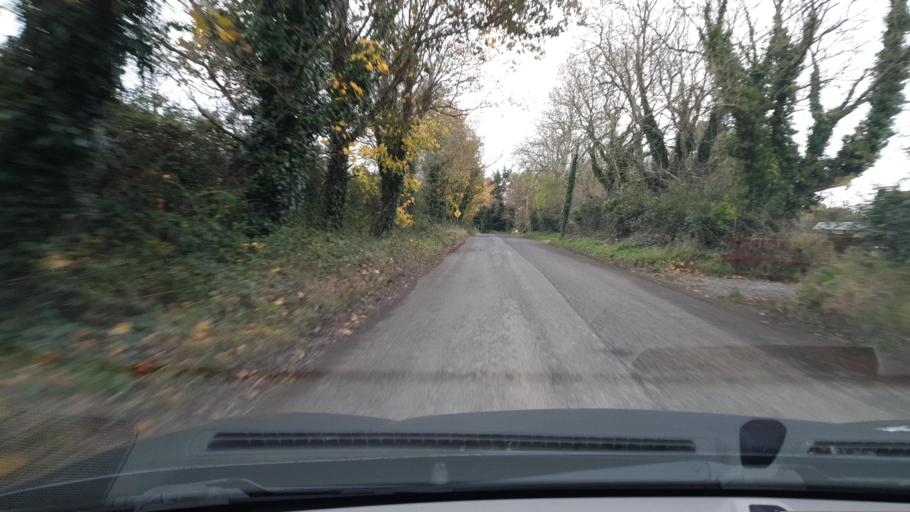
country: IE
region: Leinster
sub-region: An Mhi
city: Ashbourne
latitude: 53.5344
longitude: -6.3900
